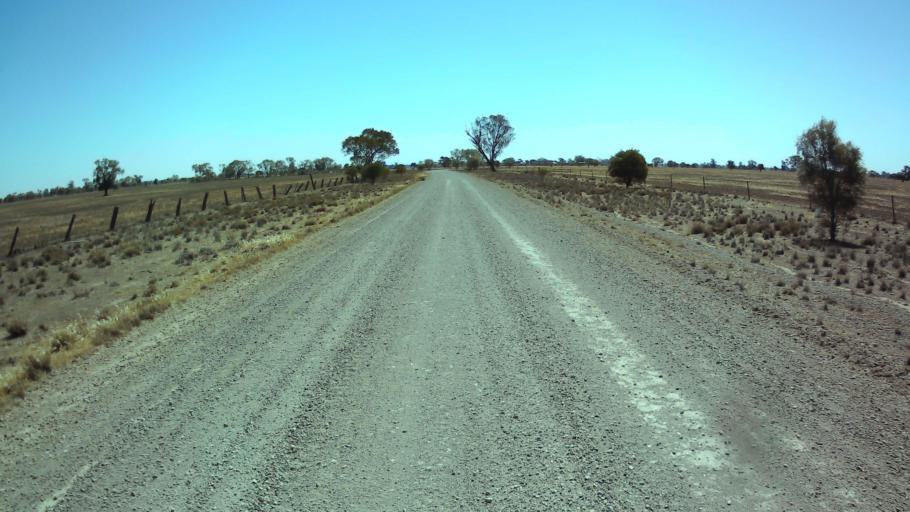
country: AU
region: New South Wales
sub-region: Forbes
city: Forbes
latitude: -33.7462
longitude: 147.7294
